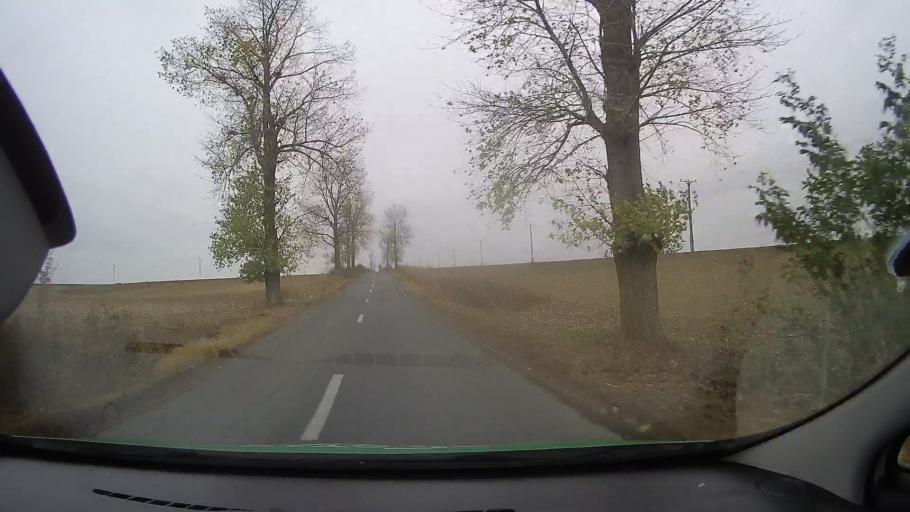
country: RO
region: Constanta
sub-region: Comuna Pantelimon
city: Pantelimon
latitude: 44.5589
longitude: 28.3230
